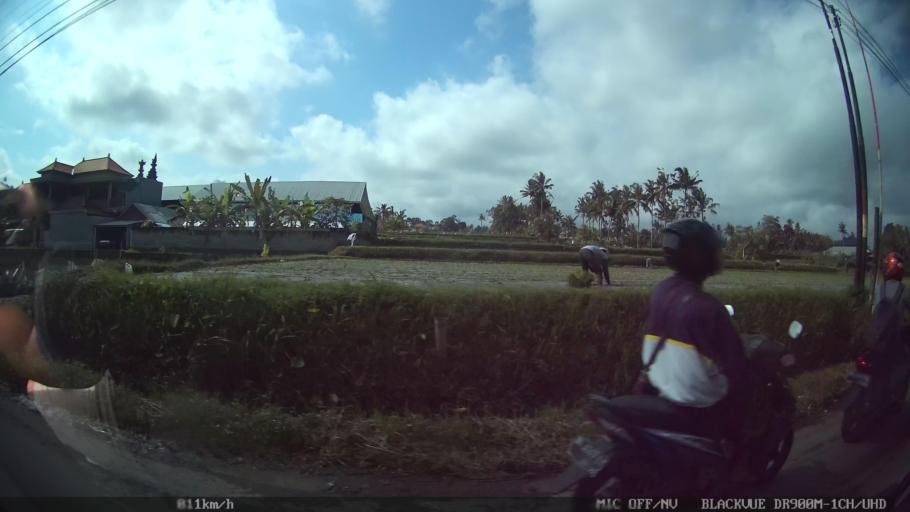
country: ID
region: Bali
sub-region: Kabupaten Gianyar
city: Ubud
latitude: -8.5103
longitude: 115.2831
